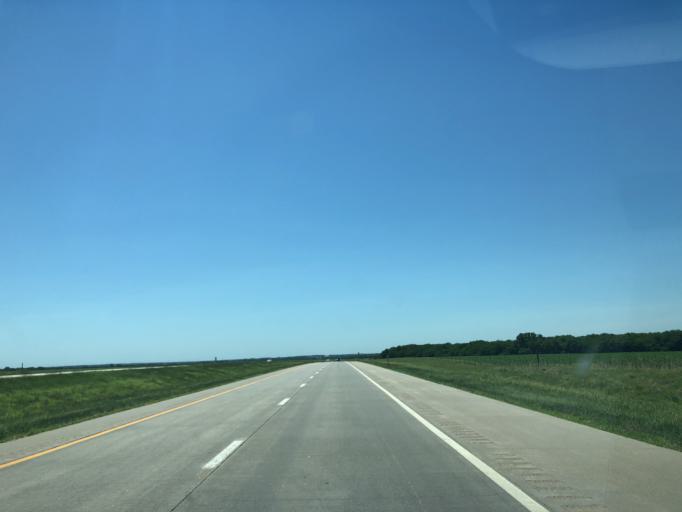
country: US
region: Kansas
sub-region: Cloud County
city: Concordia
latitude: 39.6377
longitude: -97.6605
